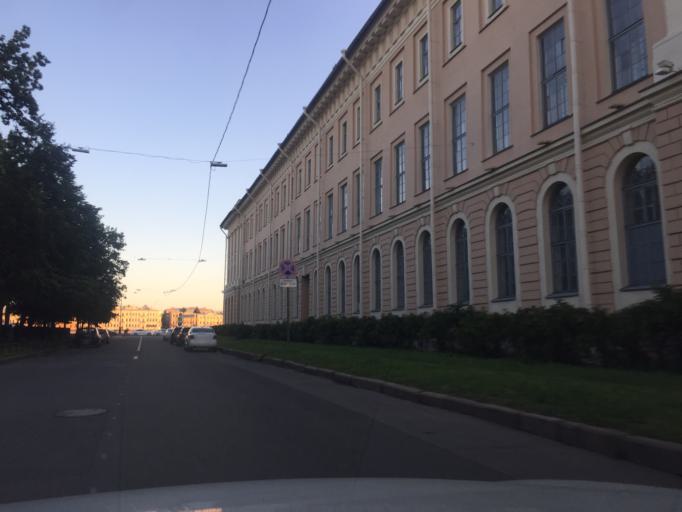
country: RU
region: St.-Petersburg
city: Saint Petersburg
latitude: 59.9387
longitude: 30.2907
